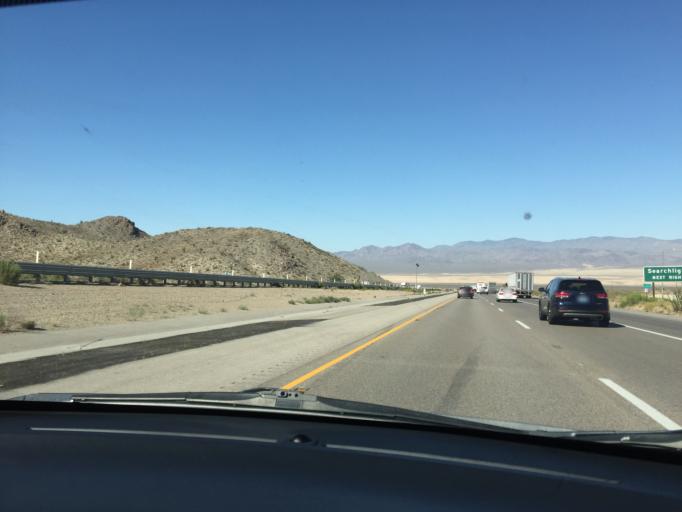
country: US
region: Nevada
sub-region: Clark County
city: Sandy Valley
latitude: 35.4668
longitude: -115.4569
